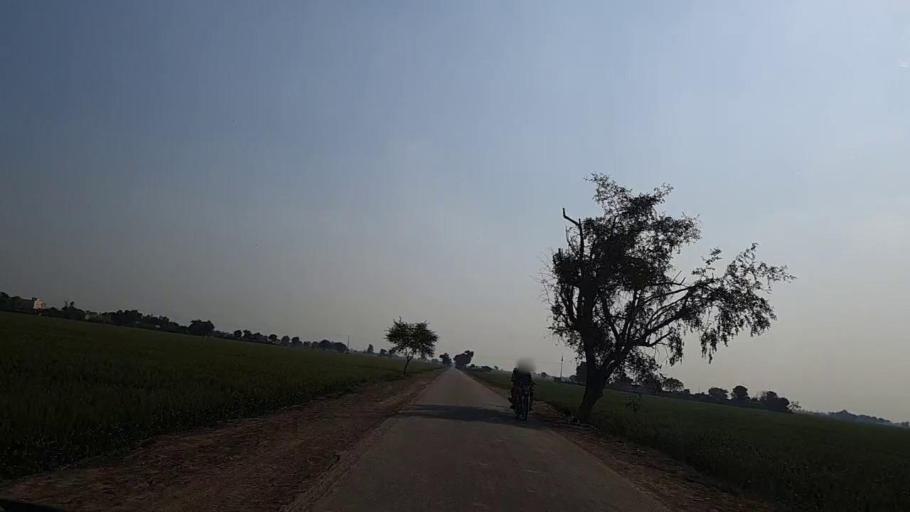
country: PK
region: Sindh
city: Sakrand
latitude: 26.0963
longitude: 68.2905
